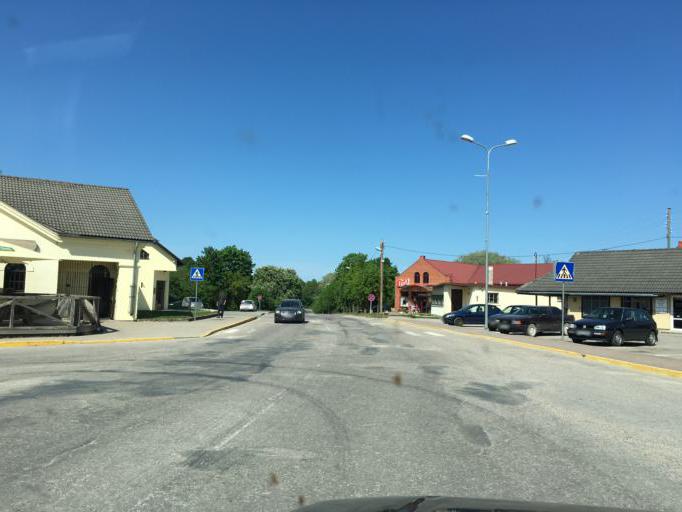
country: LV
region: Dundaga
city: Dundaga
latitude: 57.5094
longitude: 22.3505
